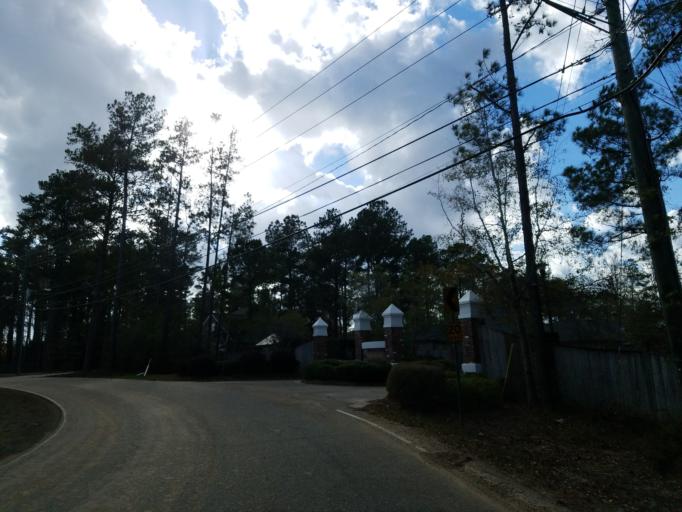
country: US
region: Mississippi
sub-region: Lamar County
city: West Hattiesburg
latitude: 31.2864
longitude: -89.3483
